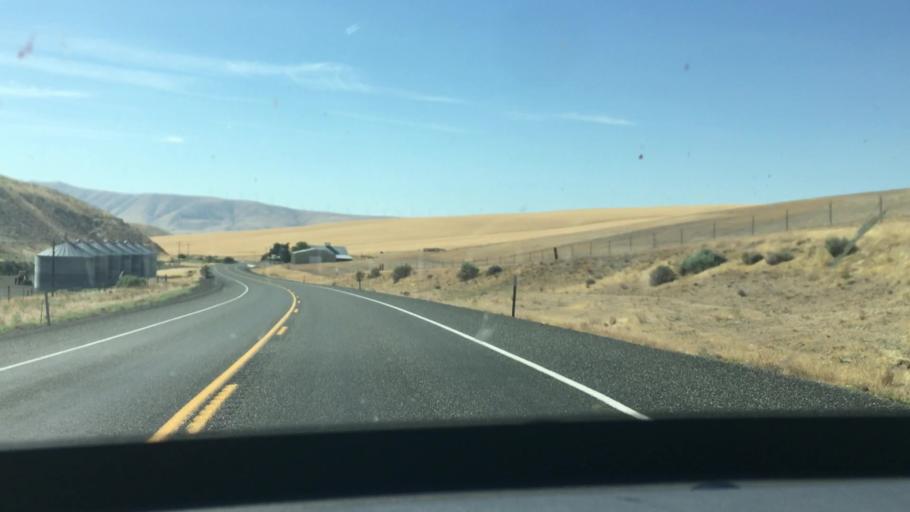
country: US
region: Oregon
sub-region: Sherman County
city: Moro
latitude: 45.6311
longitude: -120.7610
